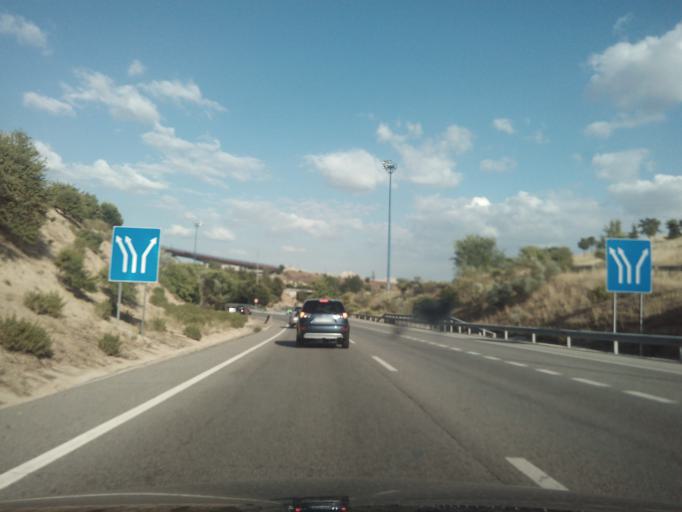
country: ES
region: Madrid
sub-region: Provincia de Madrid
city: Las Tablas
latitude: 40.5097
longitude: -3.6621
